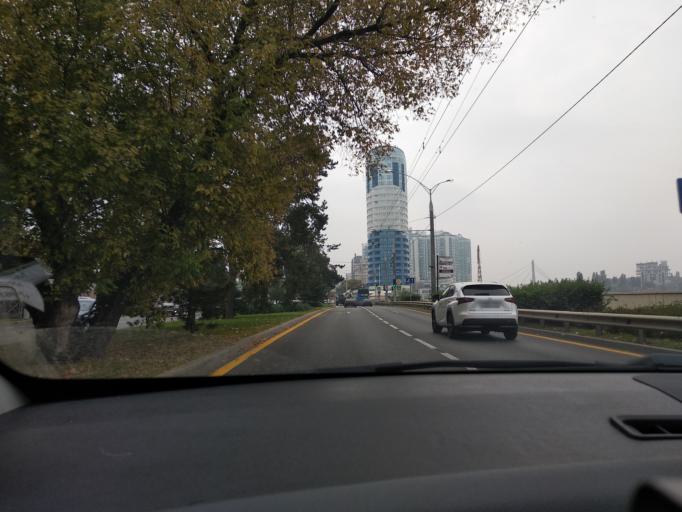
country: RU
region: Krasnodarskiy
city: Krasnodar
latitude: 45.0298
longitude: 38.9594
